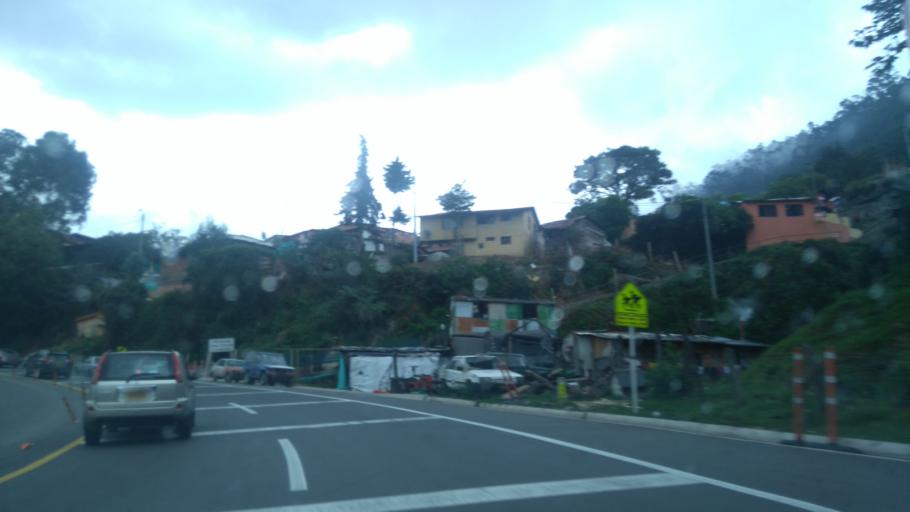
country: CO
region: Cundinamarca
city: El Rosal
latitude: 4.9041
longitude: -74.3104
